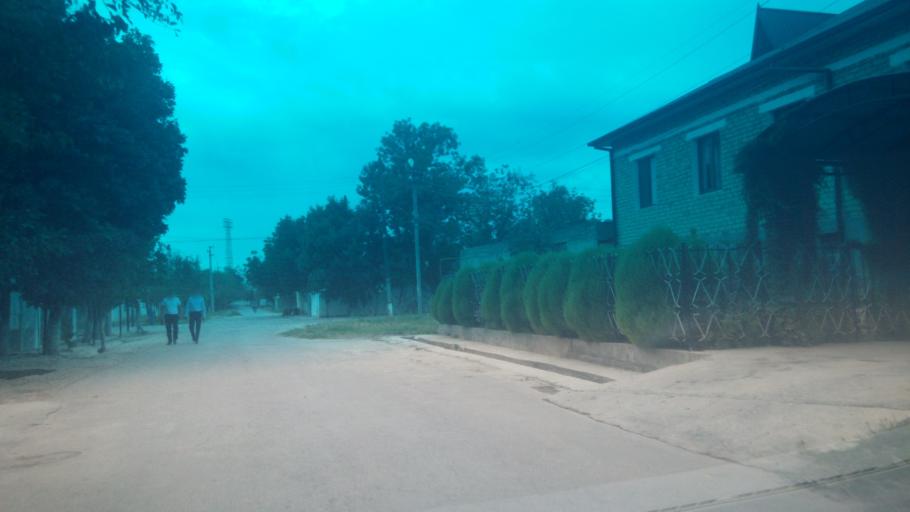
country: UZ
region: Sirdaryo
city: Guliston
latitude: 40.5026
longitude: 68.7794
